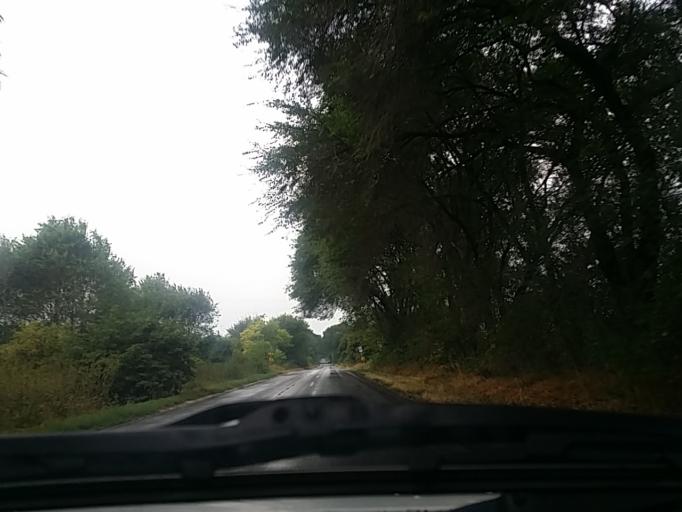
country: HU
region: Pest
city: Paty
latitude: 47.5306
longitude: 18.7851
